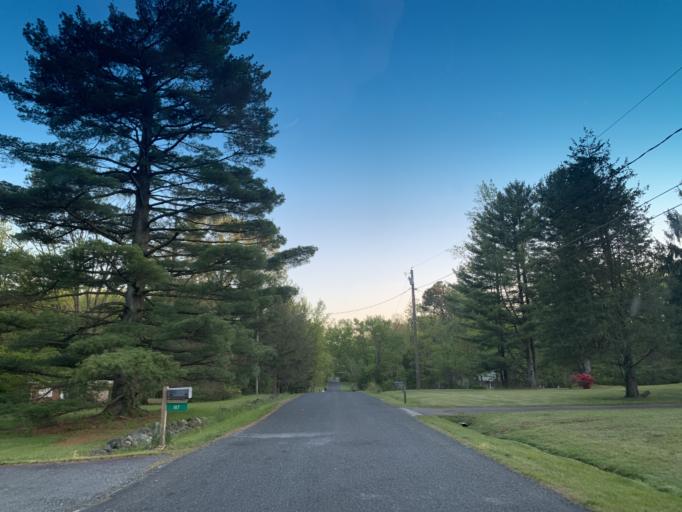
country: US
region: Maryland
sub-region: Harford County
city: Riverside
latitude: 39.5301
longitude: -76.2228
